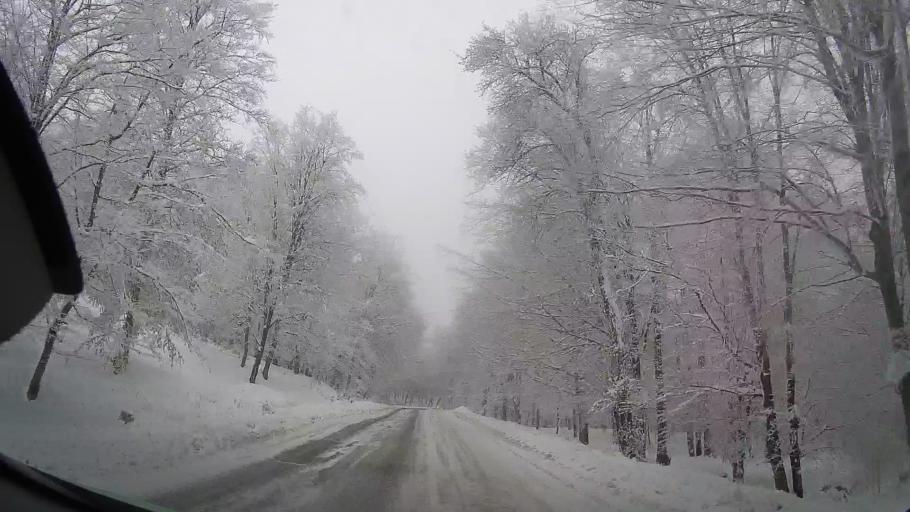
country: RO
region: Neamt
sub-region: Comuna Valea Ursului
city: Valea Ursului
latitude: 46.8380
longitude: 27.0693
